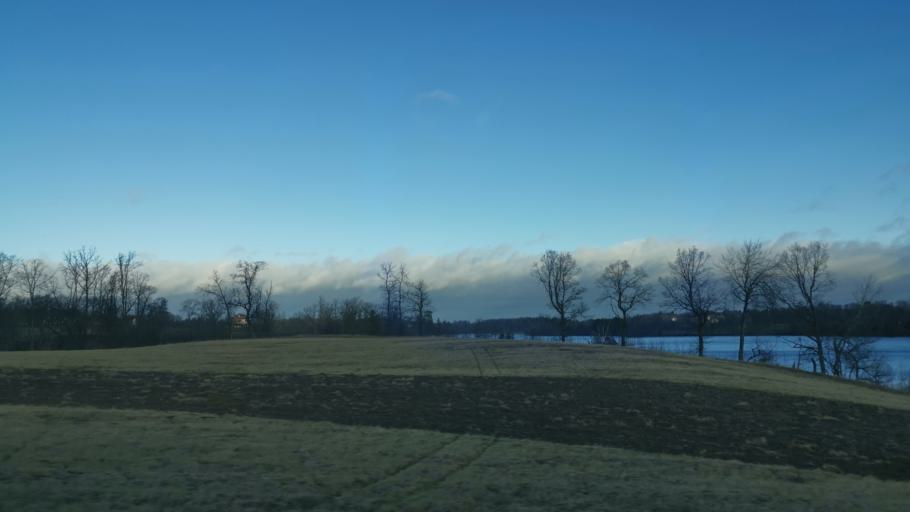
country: SE
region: Soedermanland
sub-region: Strangnas Kommun
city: Akers Styckebruk
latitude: 59.0870
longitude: 16.9839
